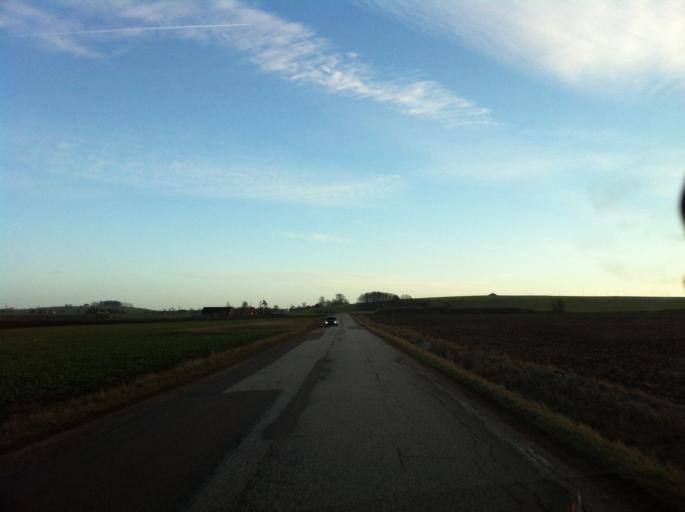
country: SE
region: Skane
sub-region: Landskrona
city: Asmundtorp
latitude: 55.9302
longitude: 12.8867
